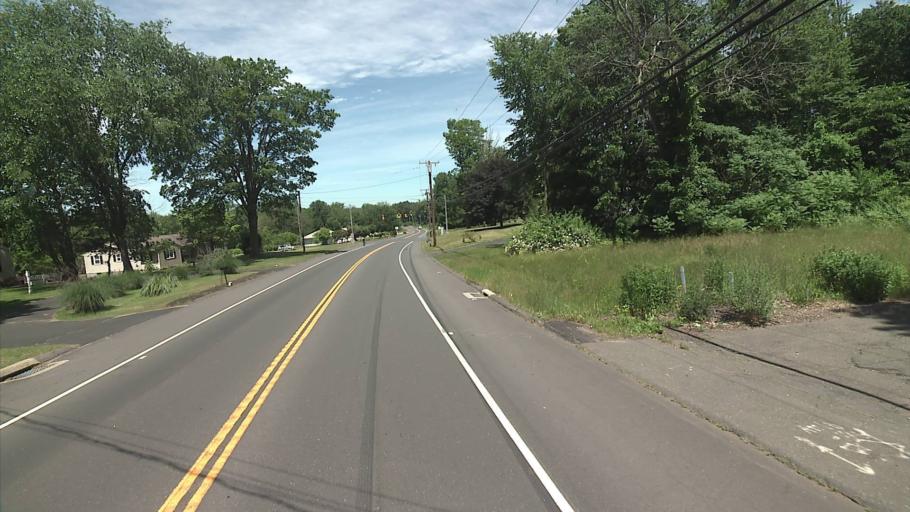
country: US
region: Connecticut
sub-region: New Haven County
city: Meriden
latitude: 41.5664
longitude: -72.8545
